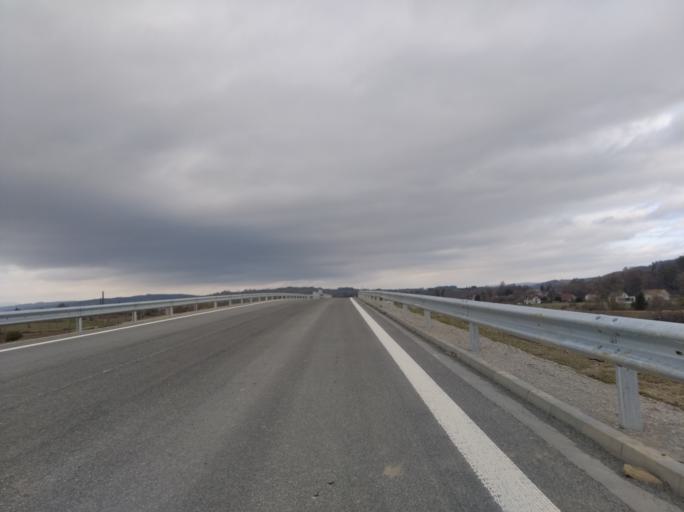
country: PL
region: Subcarpathian Voivodeship
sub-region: Powiat strzyzowski
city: Strzyzow
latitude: 49.8686
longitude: 21.7696
